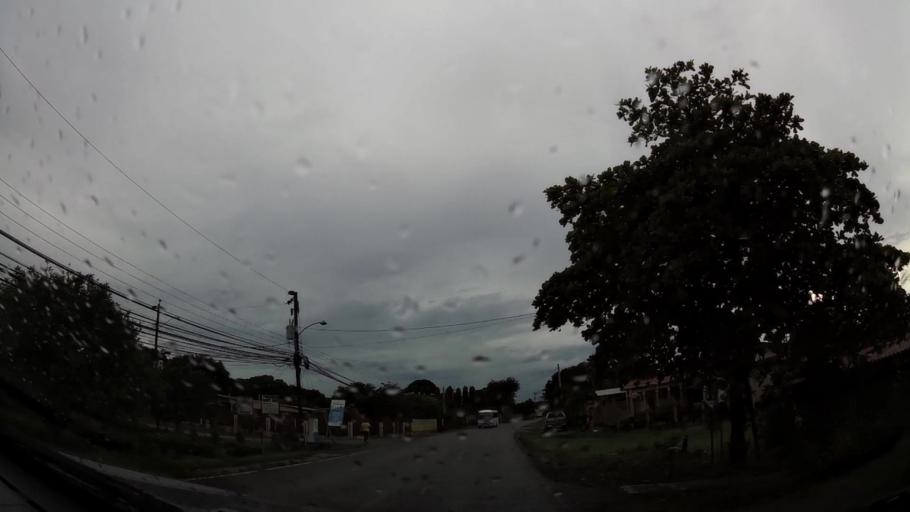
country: PA
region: Veraguas
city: Santiago de Veraguas
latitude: 8.0902
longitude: -80.9864
